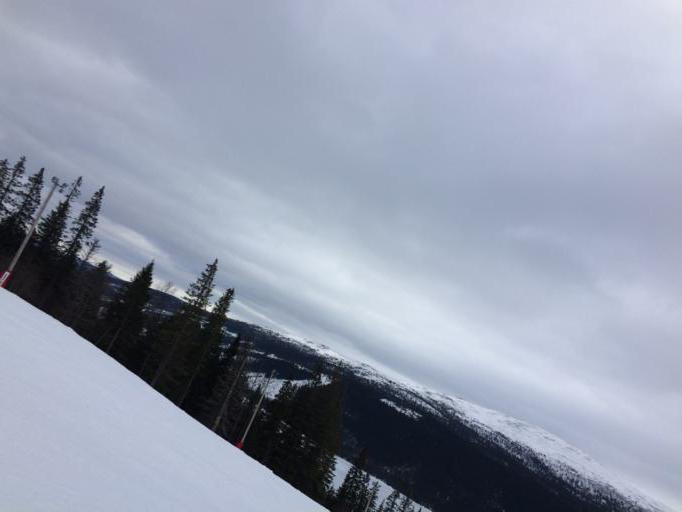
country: SE
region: Jaemtland
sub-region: Are Kommun
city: Are
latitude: 63.4092
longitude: 13.0567
